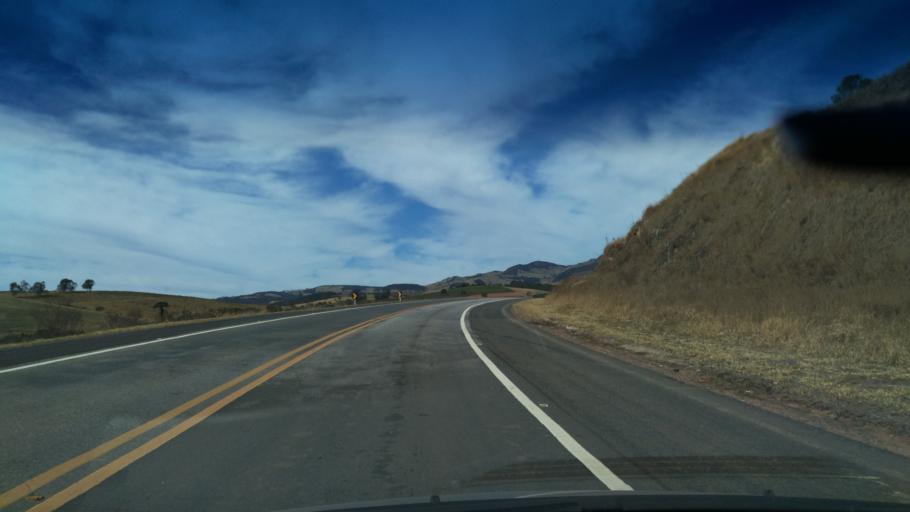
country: BR
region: Minas Gerais
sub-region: Borda Da Mata
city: Borda da Mata
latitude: -22.0479
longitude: -46.2888
